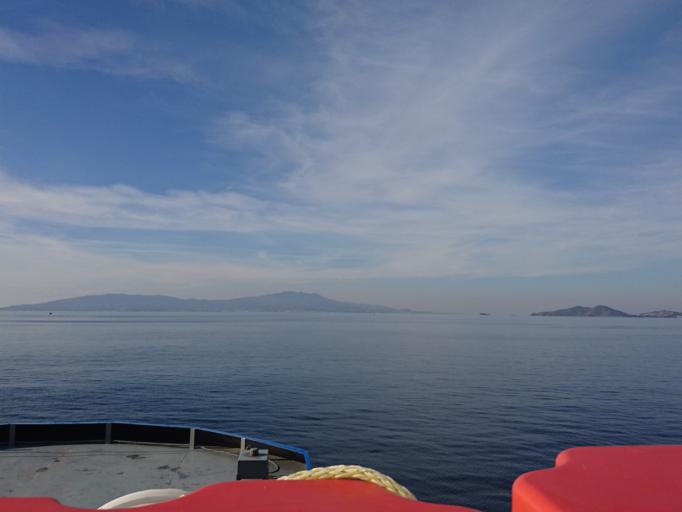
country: TR
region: Mugla
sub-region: Bodrum
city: Bodrum
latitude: 36.9915
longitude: 27.3936
